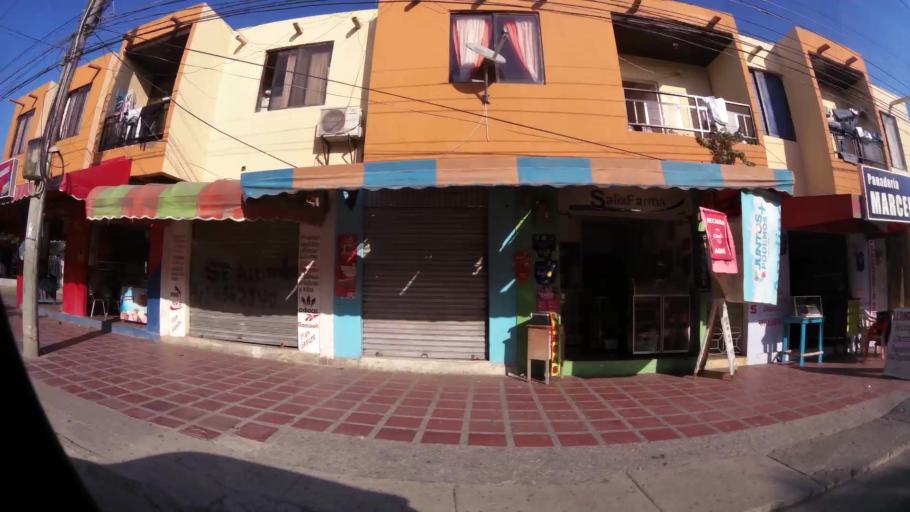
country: CO
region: Bolivar
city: Cartagena
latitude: 10.4352
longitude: -75.5152
